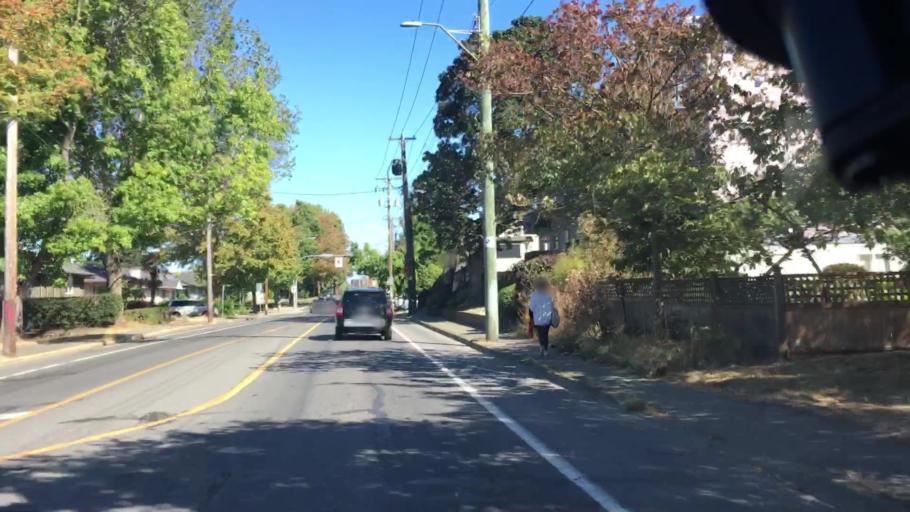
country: CA
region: British Columbia
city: Victoria
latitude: 48.4349
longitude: -123.3510
